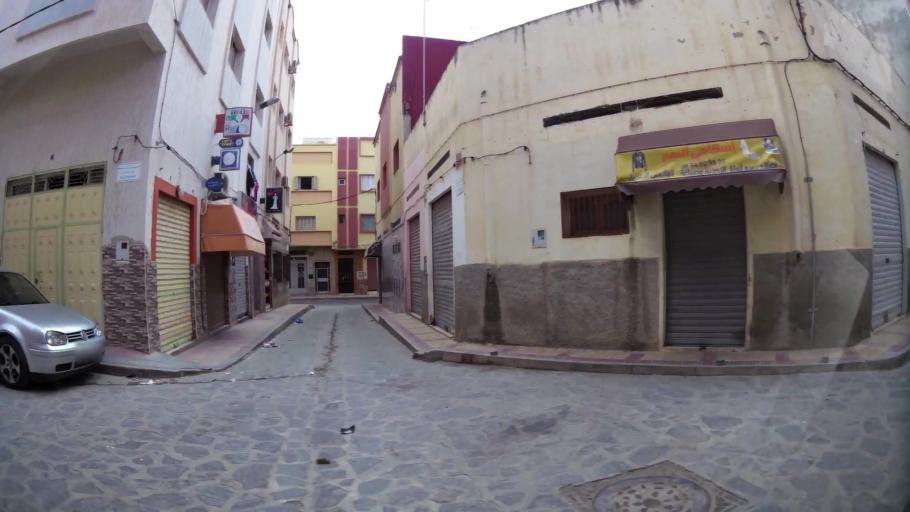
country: MA
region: Oriental
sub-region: Nador
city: Nador
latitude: 35.1692
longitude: -2.9307
